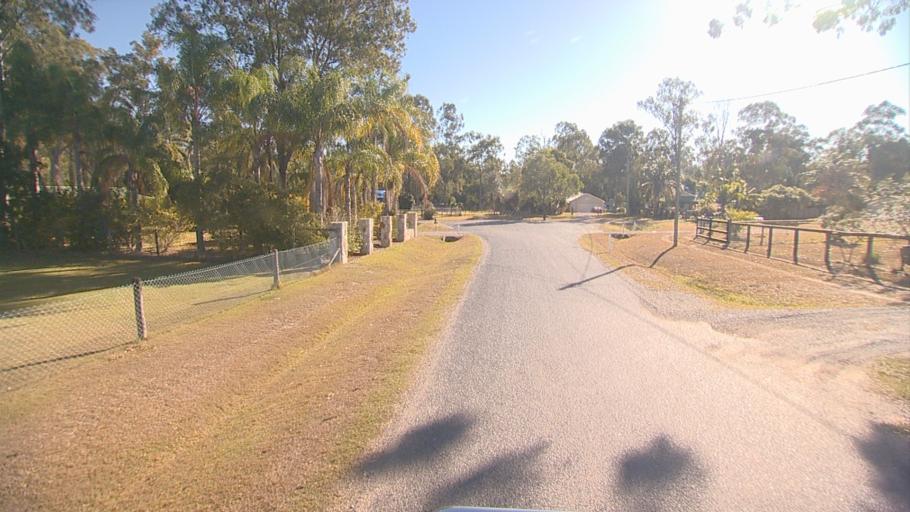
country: AU
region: Queensland
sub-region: Logan
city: North Maclean
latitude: -27.8030
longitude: 152.9786
